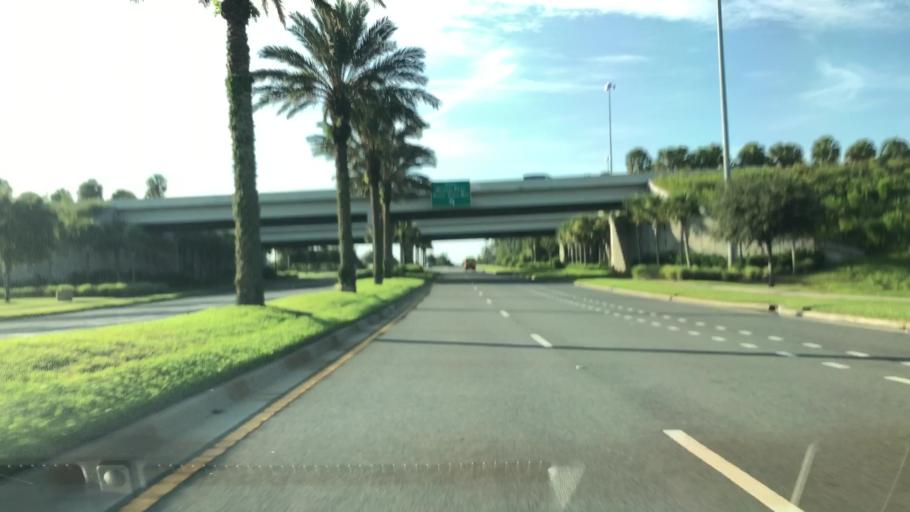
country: US
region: Florida
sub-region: Saint Johns County
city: Palm Valley
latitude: 30.1117
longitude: -81.4473
